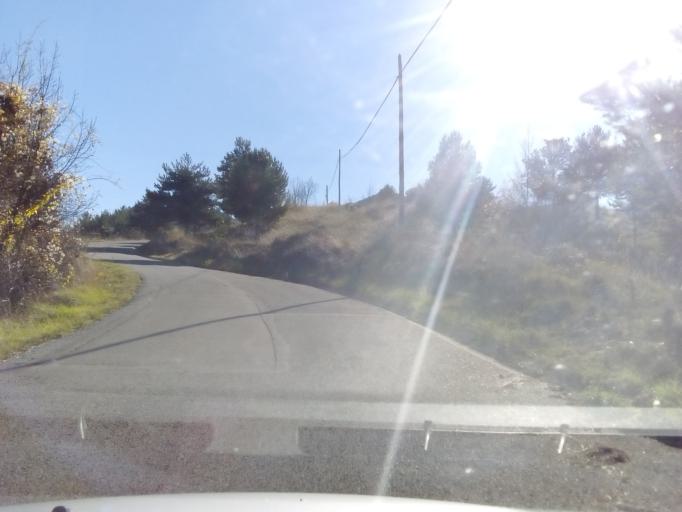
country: ES
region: Catalonia
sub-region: Provincia de Lleida
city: Bellver de Cerdanya
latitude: 42.3526
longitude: 1.7778
